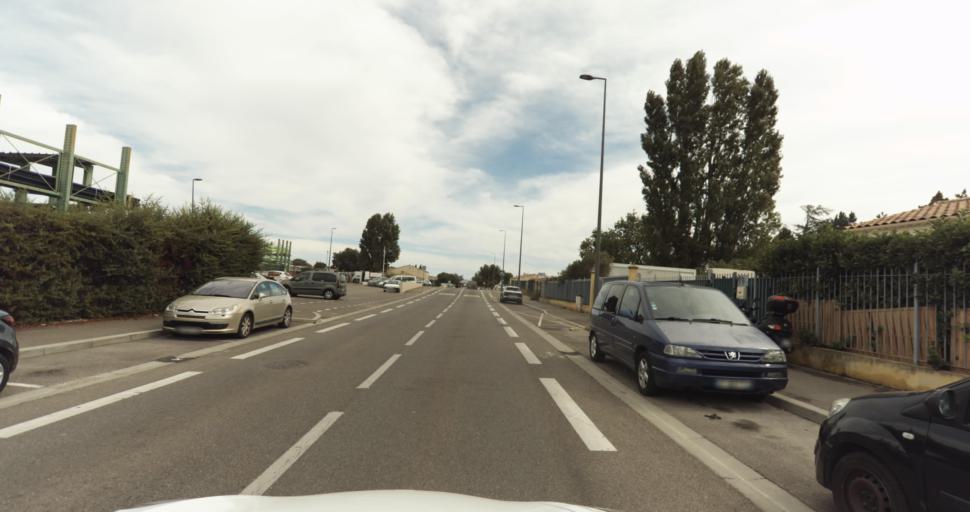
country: FR
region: Provence-Alpes-Cote d'Azur
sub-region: Departement des Bouches-du-Rhone
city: Miramas
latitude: 43.5953
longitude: 4.9965
